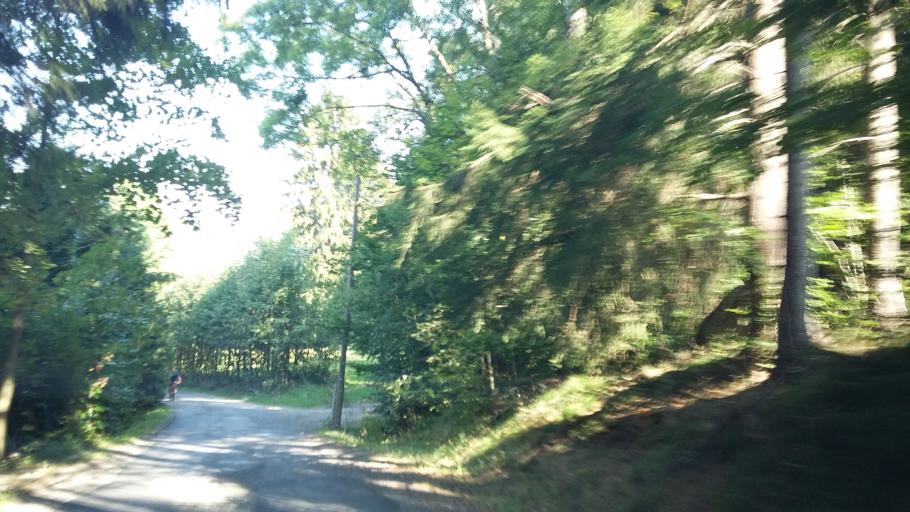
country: CZ
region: Liberecky
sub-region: Okres Jablonec nad Nisou
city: Janov nad Nisou
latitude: 50.7629
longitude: 15.1843
